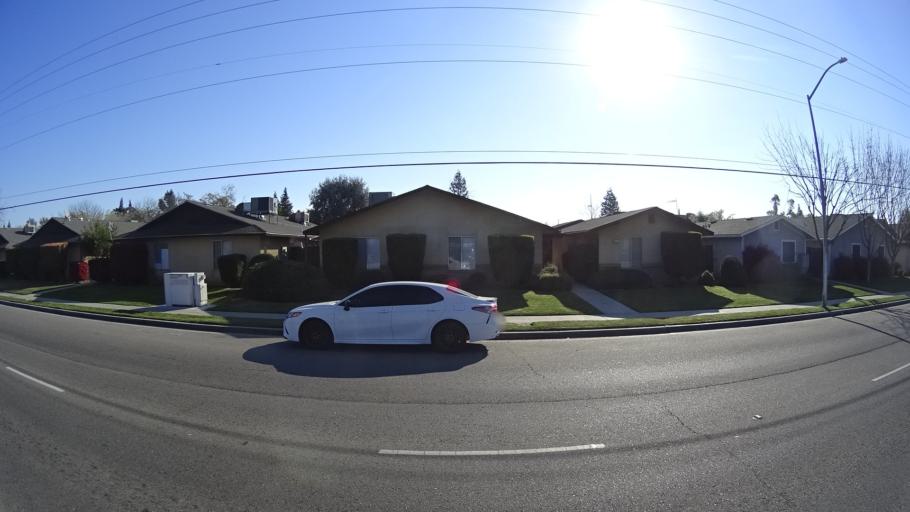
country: US
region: California
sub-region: Fresno County
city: Clovis
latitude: 36.8261
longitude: -119.7813
